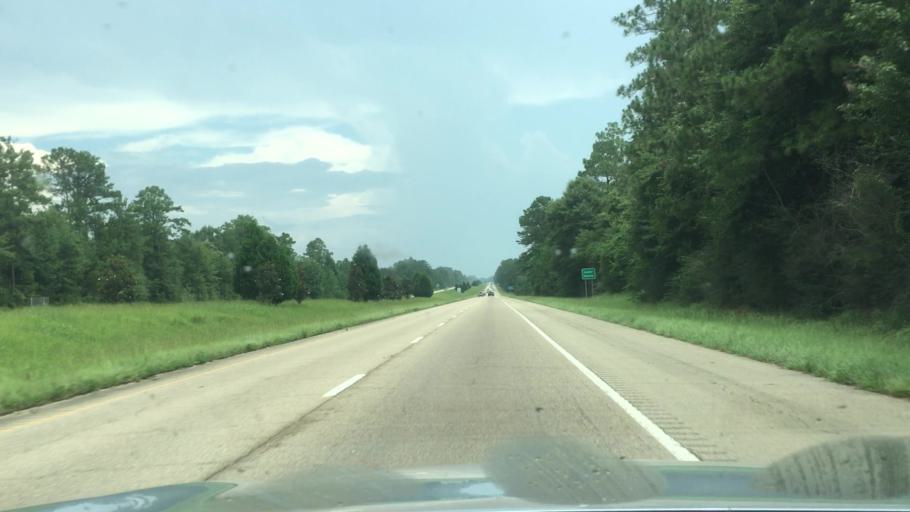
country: US
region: Mississippi
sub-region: Lamar County
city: Lumberton
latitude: 31.0093
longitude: -89.4142
